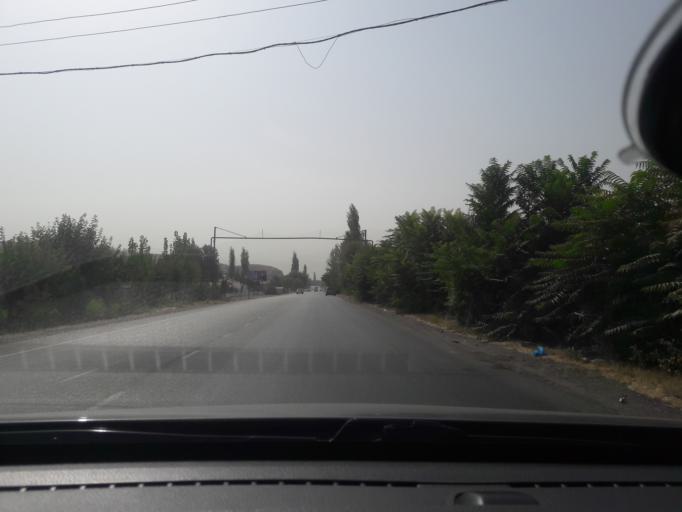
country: TJ
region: Republican Subordination
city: Vahdat
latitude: 38.5265
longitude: 69.0270
